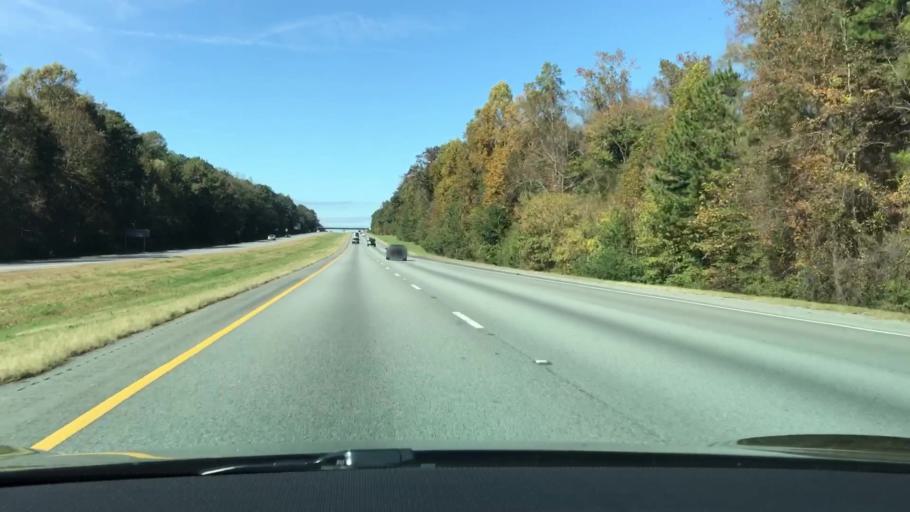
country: US
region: Georgia
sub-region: Morgan County
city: Madison
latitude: 33.5644
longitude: -83.5056
